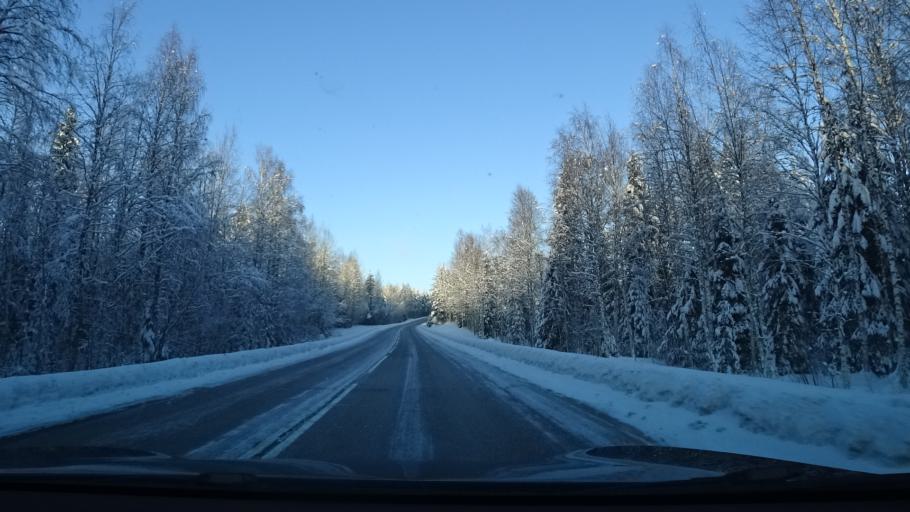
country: FI
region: Northern Savo
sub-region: Varkaus
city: Kangaslampi
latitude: 62.4250
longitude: 28.2190
